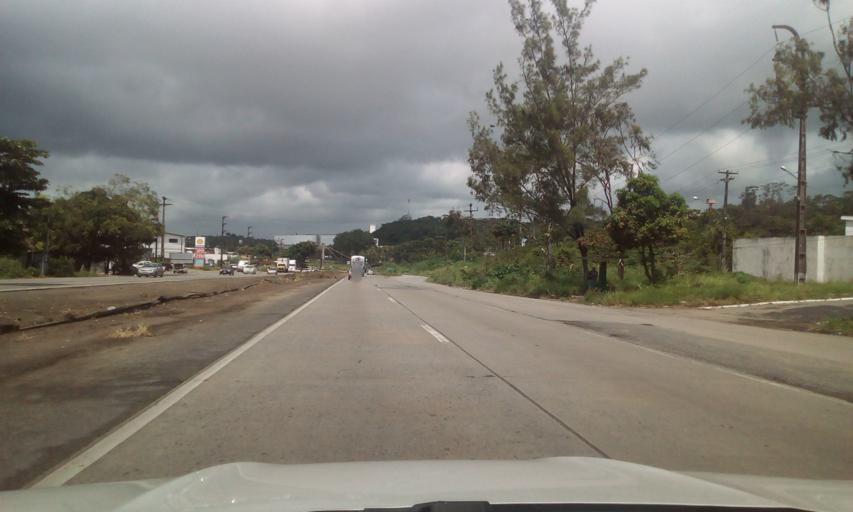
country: BR
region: Pernambuco
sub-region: Abreu E Lima
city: Abreu e Lima
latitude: -7.9296
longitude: -34.8995
